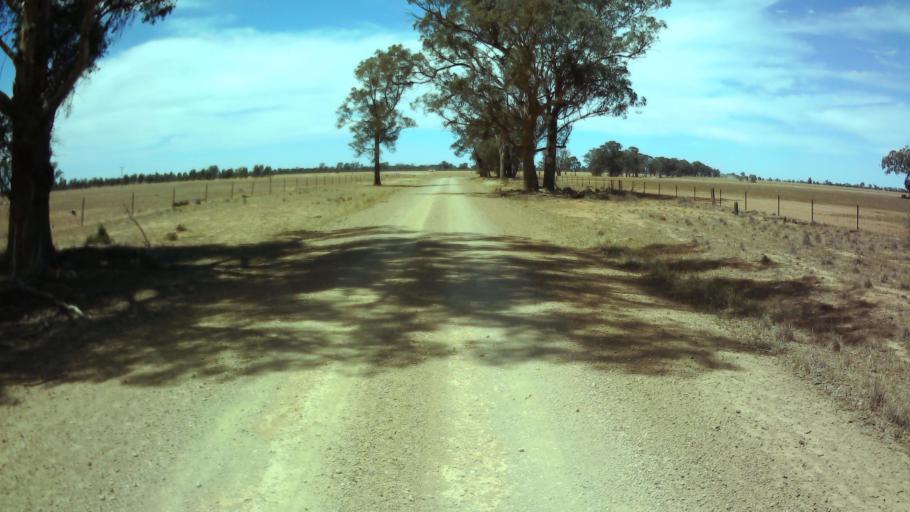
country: AU
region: New South Wales
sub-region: Weddin
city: Grenfell
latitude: -33.8630
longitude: 147.8067
